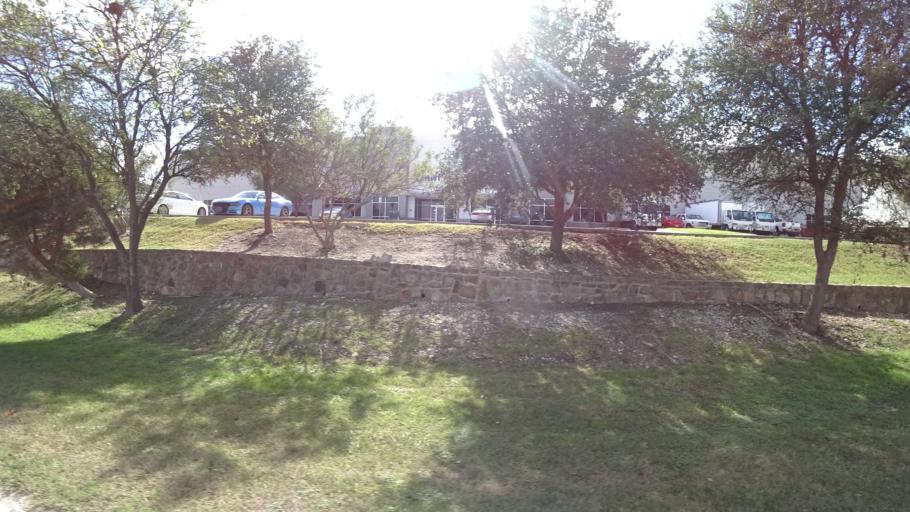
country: US
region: Texas
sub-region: Travis County
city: Windemere
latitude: 30.4678
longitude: -97.6651
